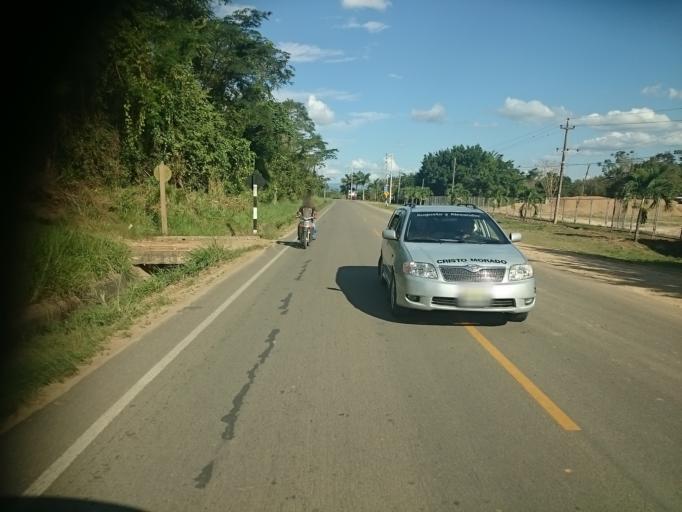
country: PE
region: San Martin
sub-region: Provincia de San Martin
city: Tarapoto
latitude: -6.4662
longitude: -76.4150
